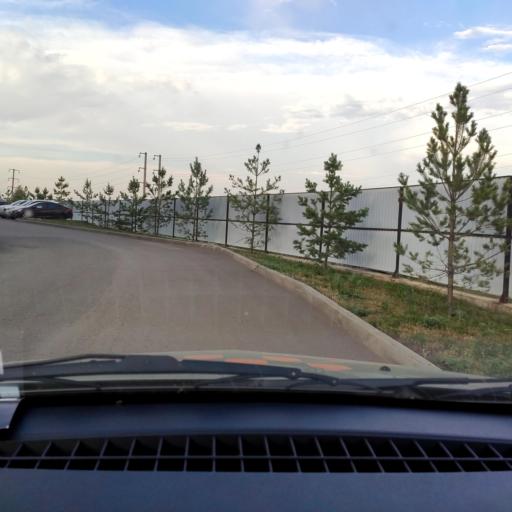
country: RU
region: Bashkortostan
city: Ufa
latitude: 54.5879
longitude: 55.9165
